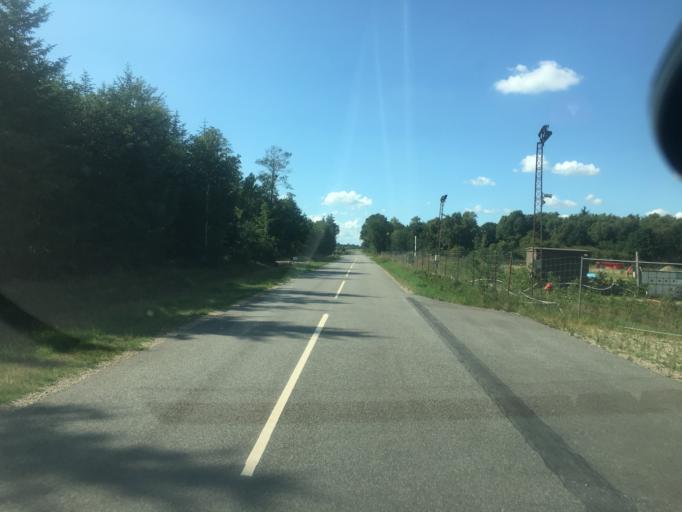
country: DE
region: Schleswig-Holstein
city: Ellhoft
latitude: 54.9656
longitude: 8.9760
